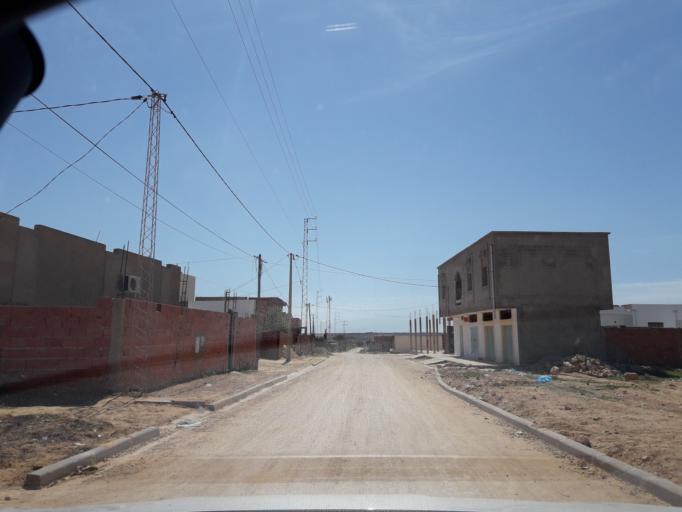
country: TN
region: Safaqis
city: Sfax
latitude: 34.7442
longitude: 10.5124
